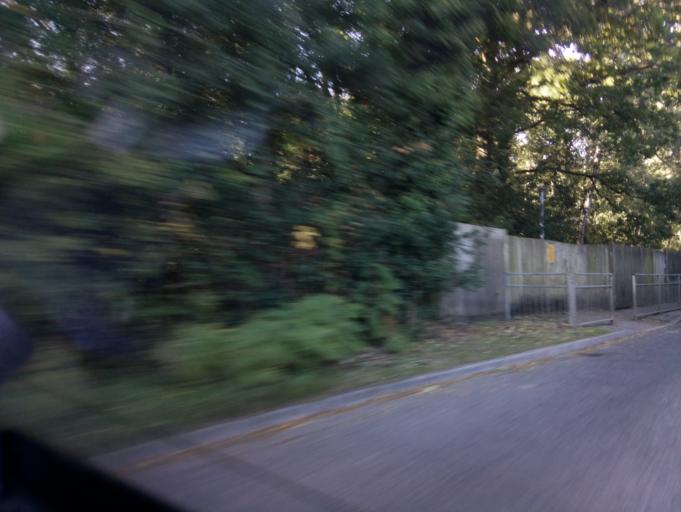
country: GB
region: England
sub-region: West Berkshire
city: Cold Ash
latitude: 51.4340
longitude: -1.2702
